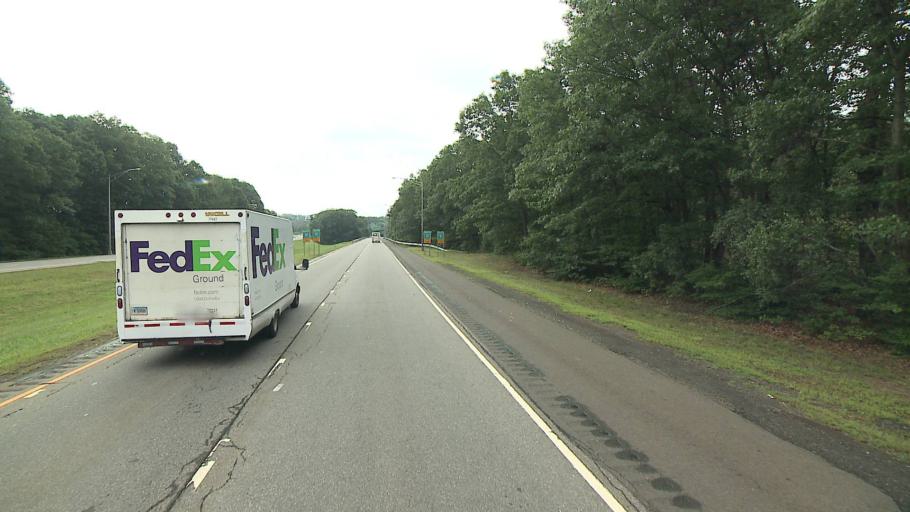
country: US
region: Connecticut
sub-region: New Haven County
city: Wallingford Center
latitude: 41.4263
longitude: -72.8300
